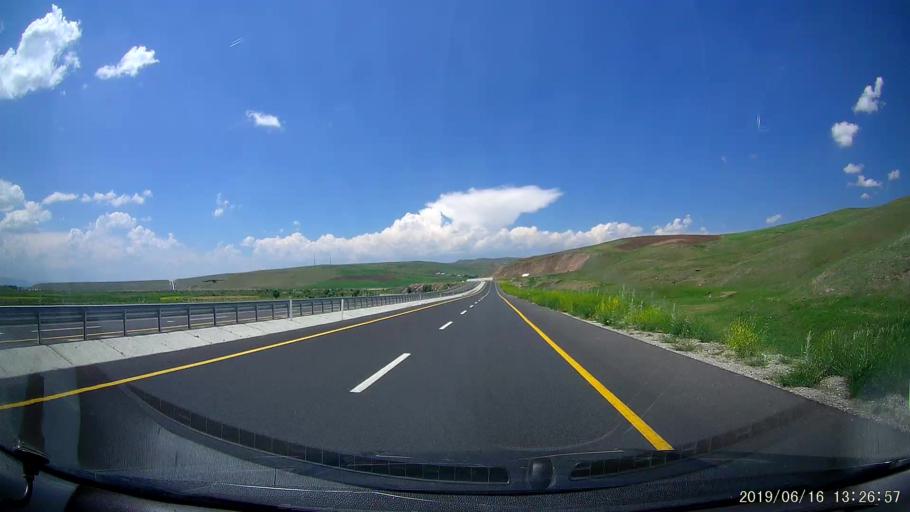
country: TR
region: Agri
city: Taslicay
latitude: 39.6644
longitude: 43.3179
